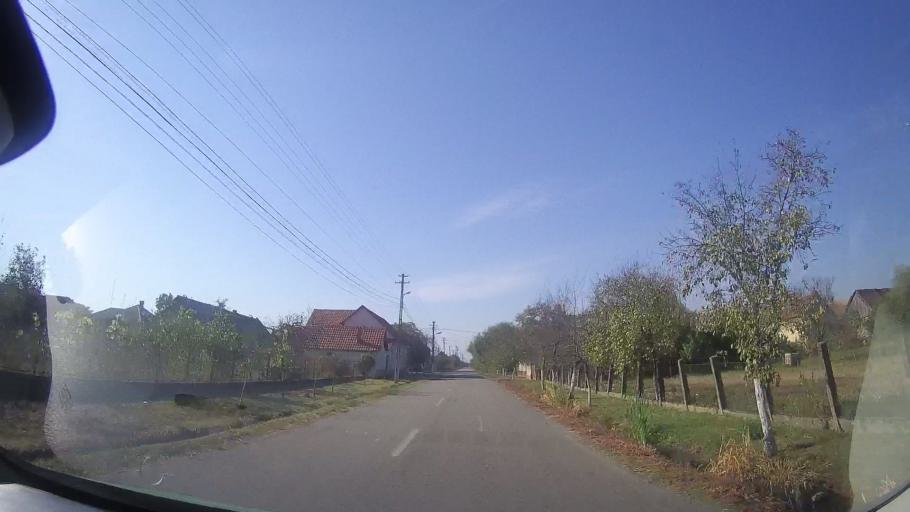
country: RO
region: Timis
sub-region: Comuna Topolovatu Mare
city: Topolovatu Mare
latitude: 45.7915
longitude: 21.5852
